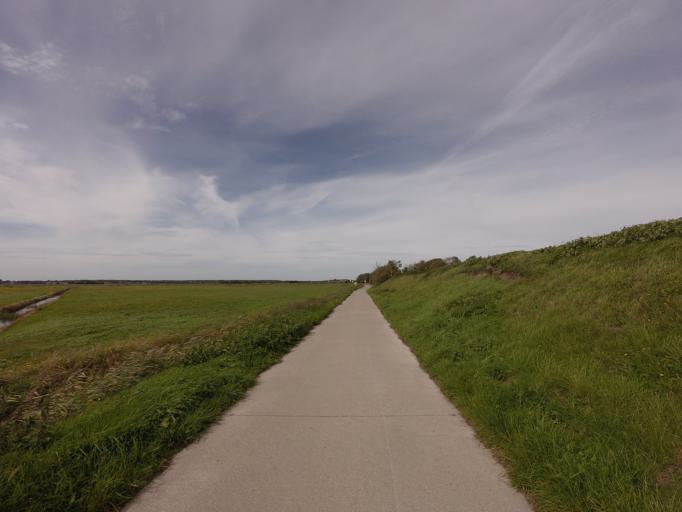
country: NL
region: North Holland
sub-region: Gemeente Texel
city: Den Burg
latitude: 53.0758
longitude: 4.7885
